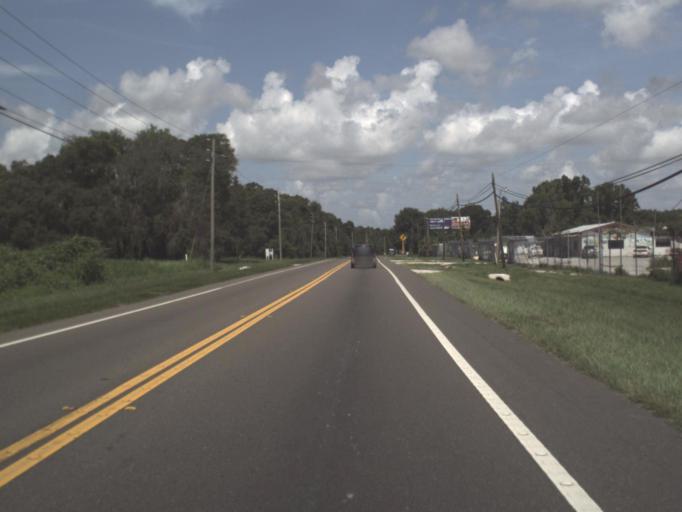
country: US
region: Florida
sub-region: Pasco County
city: Shady Hills
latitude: 28.3220
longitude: -82.5077
